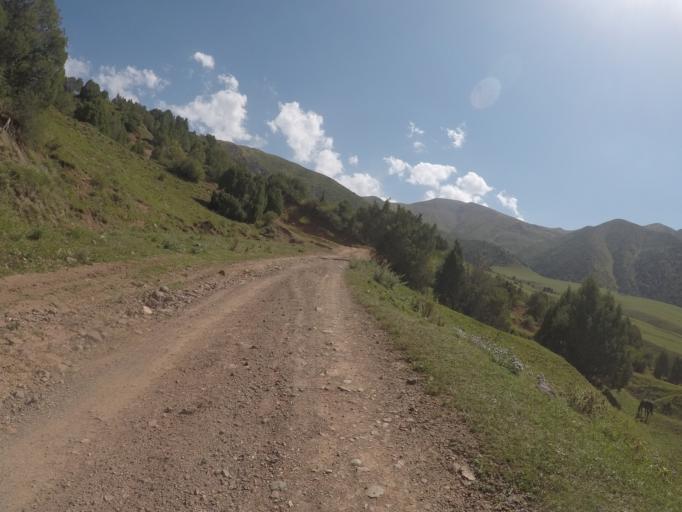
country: KG
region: Chuy
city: Bishkek
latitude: 42.6476
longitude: 74.5773
